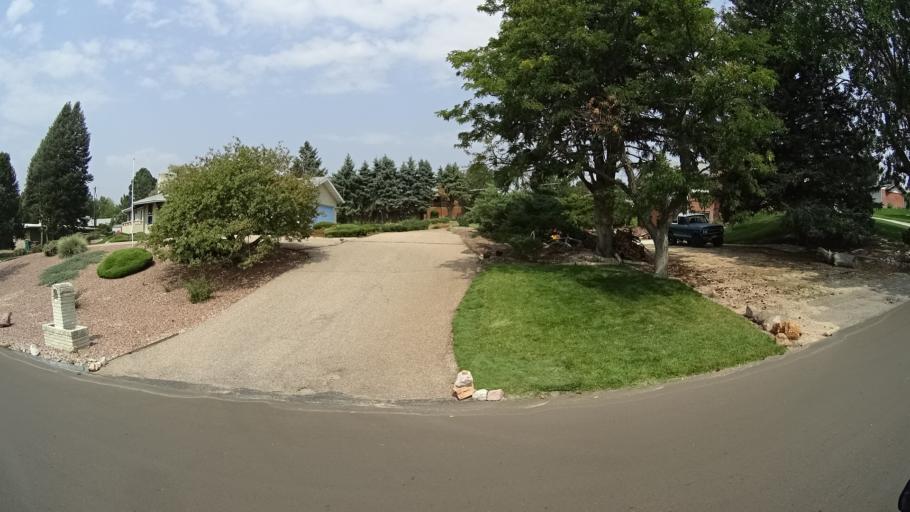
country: US
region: Colorado
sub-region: El Paso County
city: Colorado Springs
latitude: 38.8236
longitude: -104.7724
